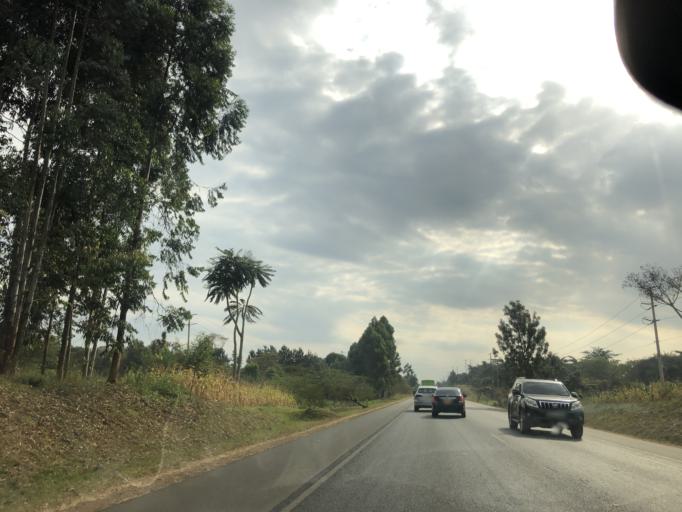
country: KE
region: Kiambu
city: Kiambu
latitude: -1.2153
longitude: 36.8574
